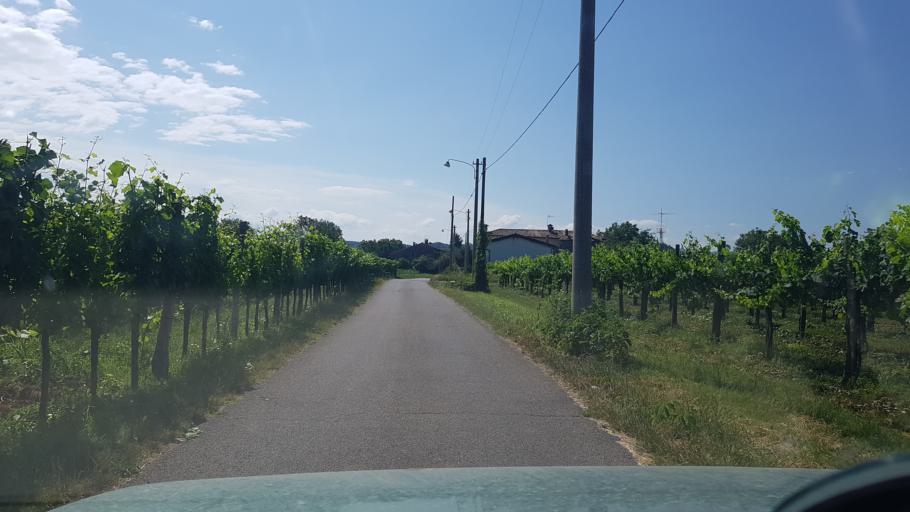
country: SI
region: Nova Gorica
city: Nova Gorica
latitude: 45.9638
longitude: 13.6287
